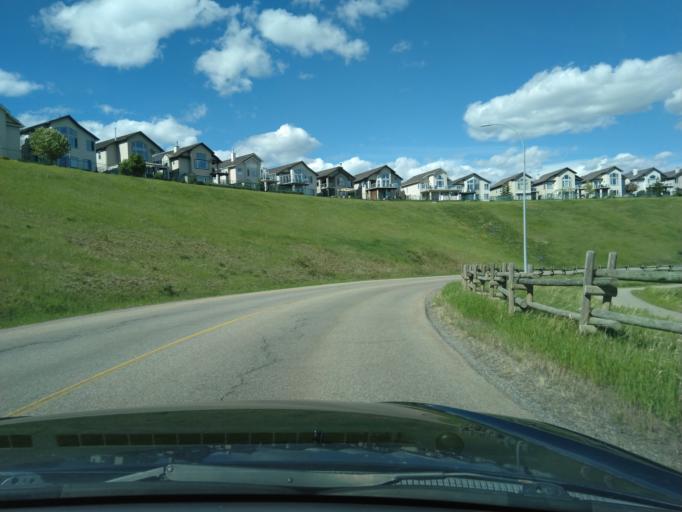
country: CA
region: Alberta
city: Cochrane
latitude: 51.1945
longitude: -114.4269
